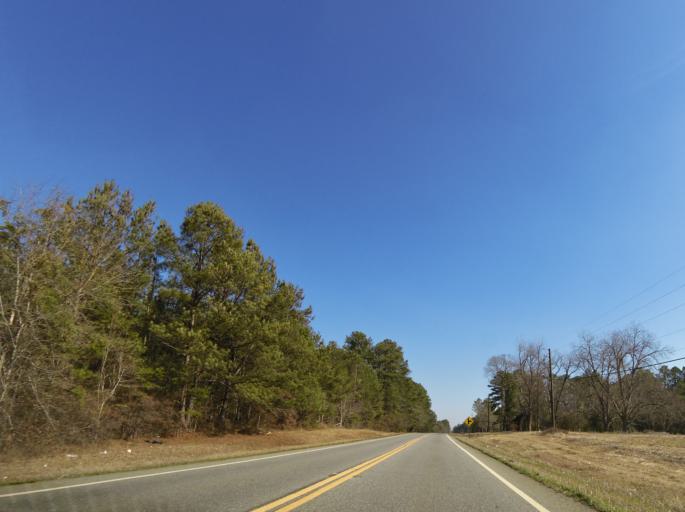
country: US
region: Georgia
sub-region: Bleckley County
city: Cochran
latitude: 32.3655
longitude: -83.3802
